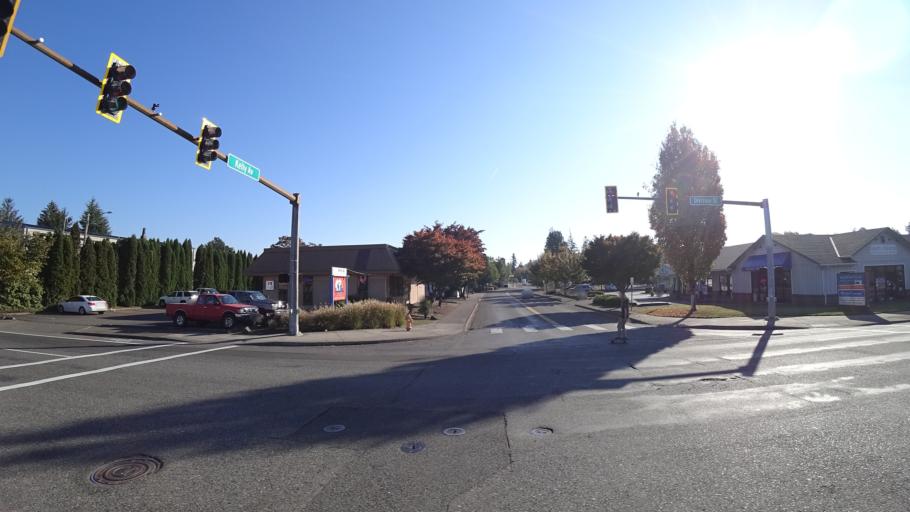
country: US
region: Oregon
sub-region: Multnomah County
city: Gresham
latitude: 45.5049
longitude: -122.4260
